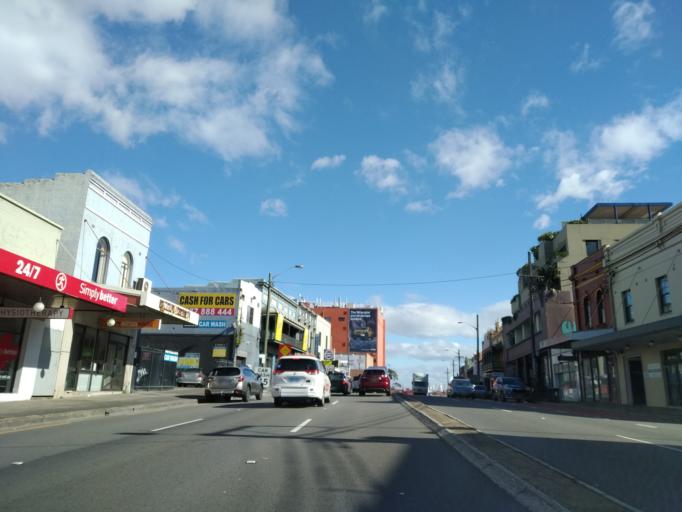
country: AU
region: New South Wales
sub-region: Marrickville
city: Lewisham
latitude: -33.8887
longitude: 151.1554
